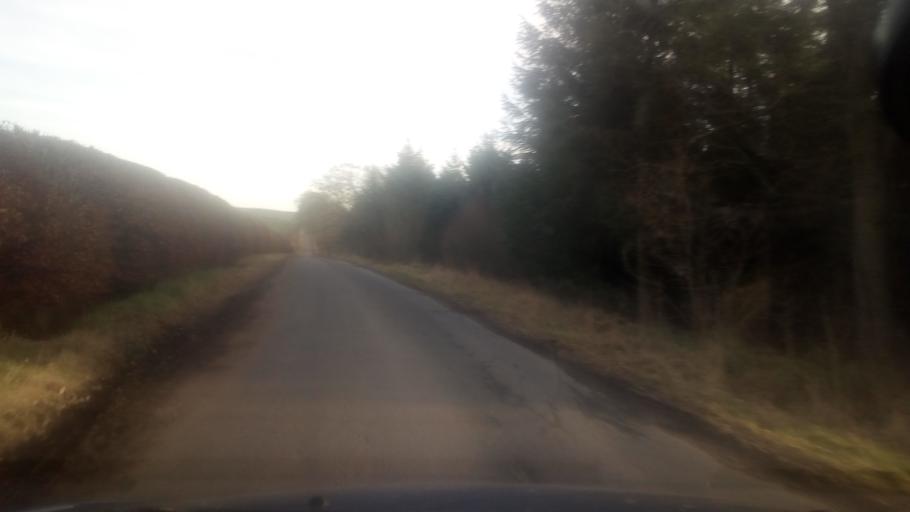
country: GB
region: Scotland
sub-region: The Scottish Borders
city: Jedburgh
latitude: 55.4147
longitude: -2.6172
